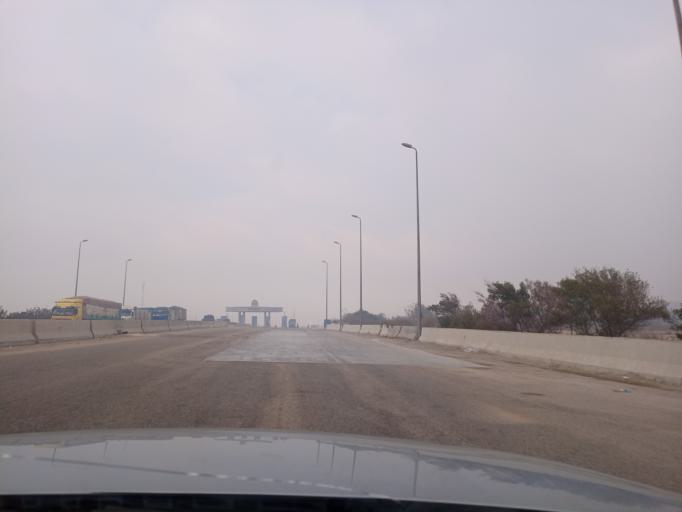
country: EG
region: Al Jizah
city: Al `Ayyat
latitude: 29.6833
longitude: 31.2276
